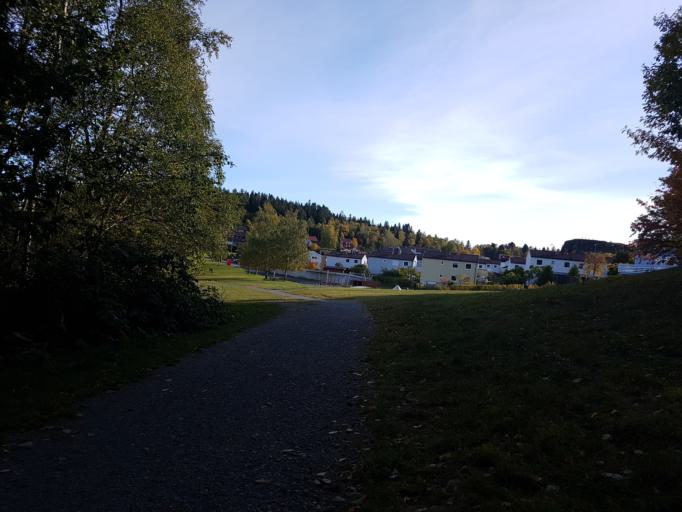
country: NO
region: Sor-Trondelag
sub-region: Trondheim
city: Trondheim
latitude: 63.4248
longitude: 10.3531
